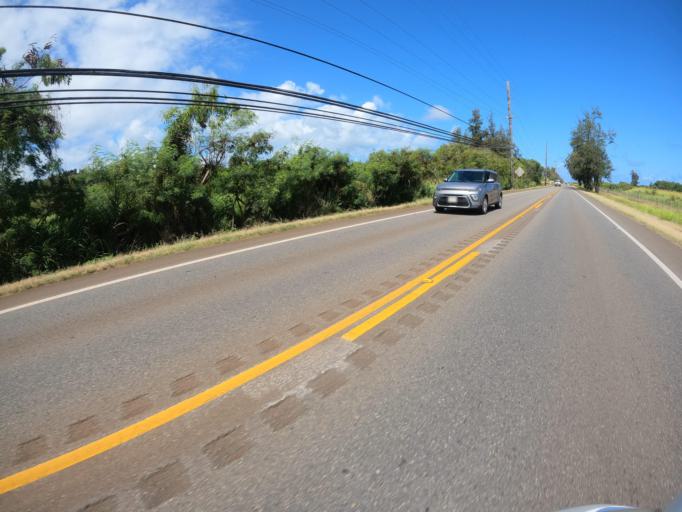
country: US
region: Hawaii
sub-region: Honolulu County
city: Kahuku
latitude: 21.6783
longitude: -157.9544
